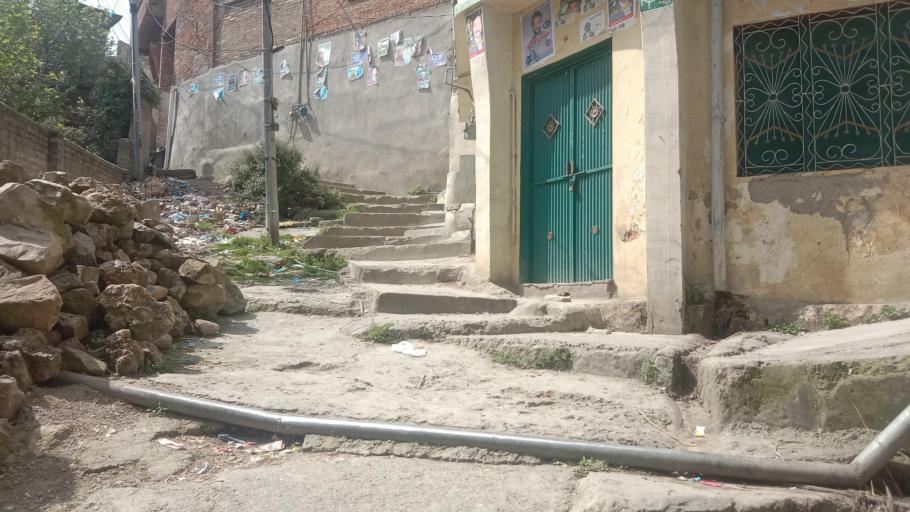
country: PK
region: Khyber Pakhtunkhwa
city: Abbottabad
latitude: 34.1303
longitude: 73.2004
